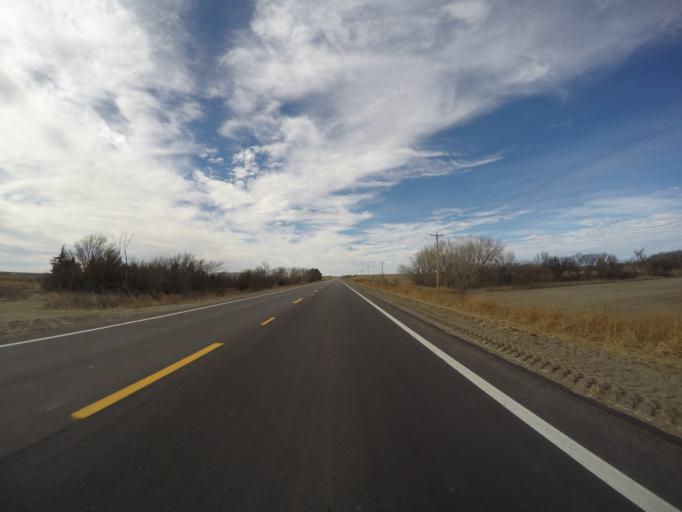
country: US
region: Nebraska
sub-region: Franklin County
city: Franklin
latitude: 40.0962
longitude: -98.8506
